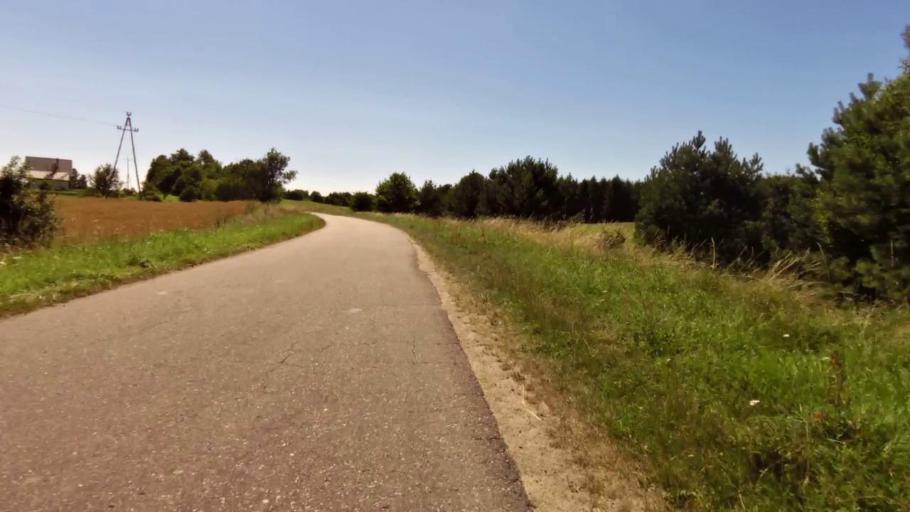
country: PL
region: West Pomeranian Voivodeship
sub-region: Powiat szczecinecki
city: Bialy Bor
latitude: 53.9316
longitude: 16.8521
